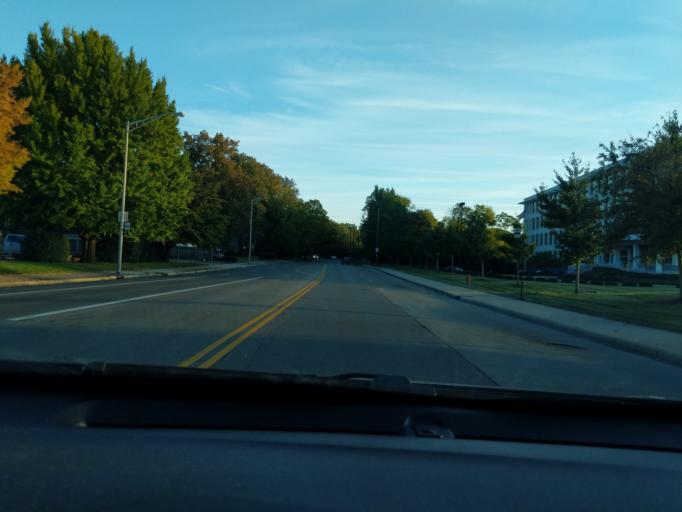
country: US
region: Ohio
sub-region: Montgomery County
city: Oakwood
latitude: 39.7375
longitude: -84.1859
